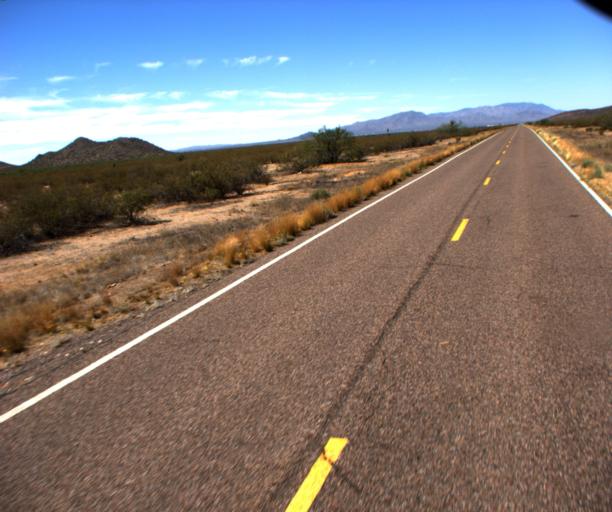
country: US
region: Arizona
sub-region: Yavapai County
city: Congress
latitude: 34.0317
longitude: -113.0819
